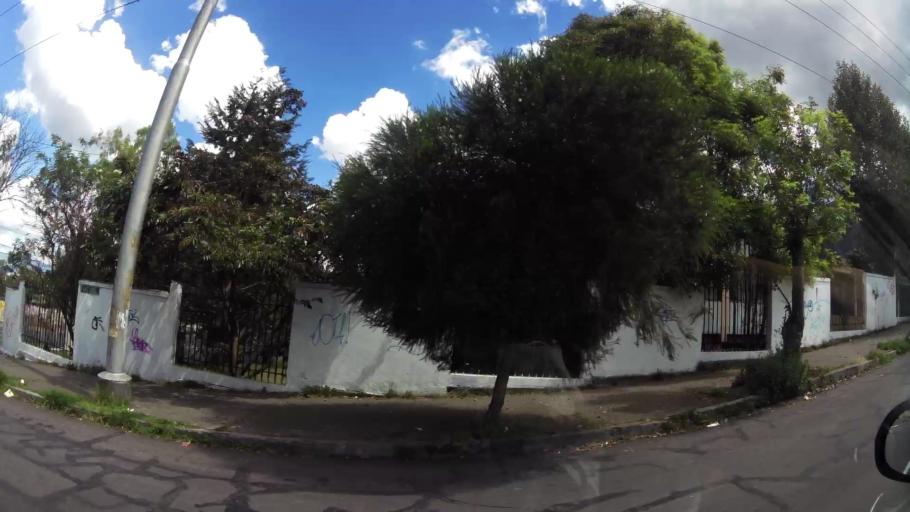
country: EC
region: Pichincha
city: Quito
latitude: -0.1885
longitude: -78.5056
